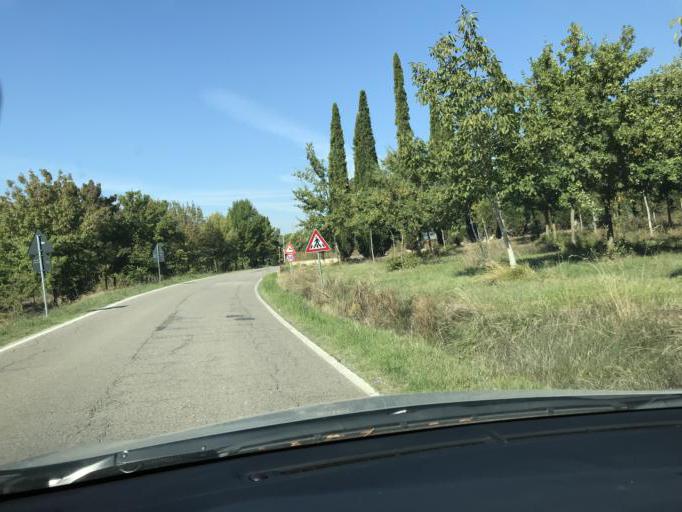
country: IT
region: Umbria
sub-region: Provincia di Perugia
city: Via Lippia
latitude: 43.1044
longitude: 12.4801
